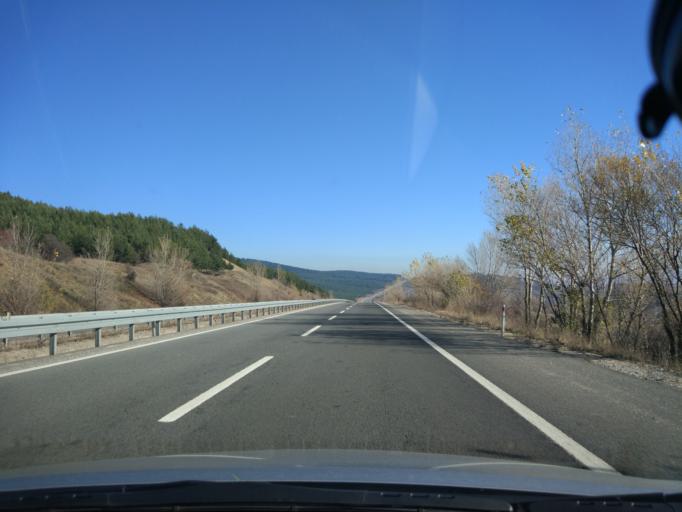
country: TR
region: Bolu
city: Gerede
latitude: 40.8256
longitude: 32.3467
